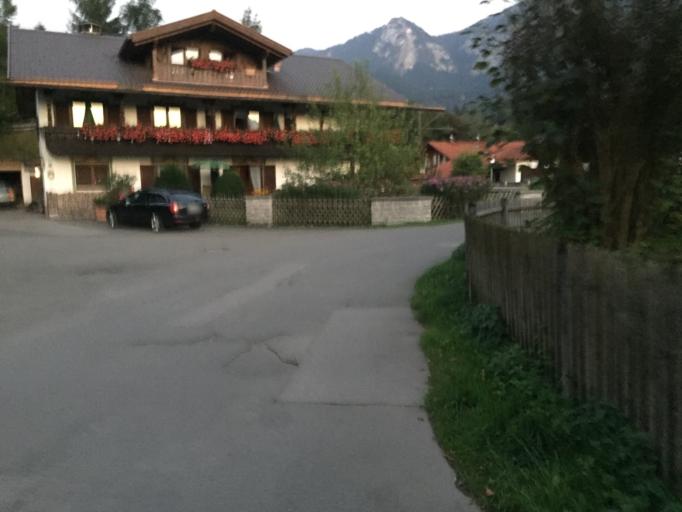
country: DE
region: Bavaria
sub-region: Upper Bavaria
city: Grainau
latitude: 47.4716
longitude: 11.0292
